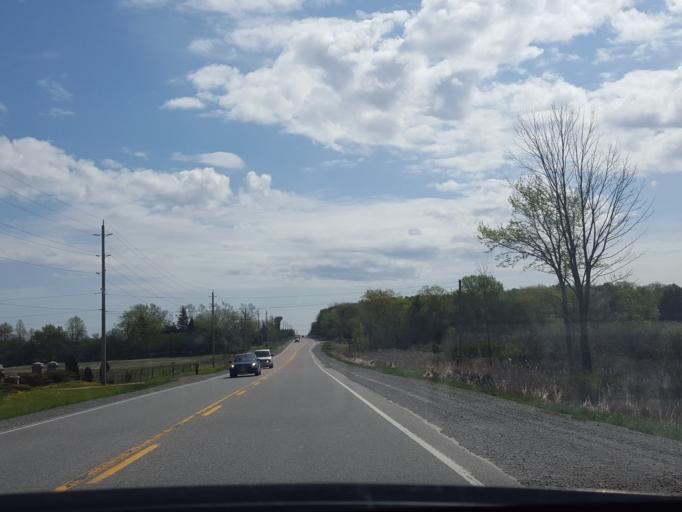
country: CA
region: Ontario
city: Oshawa
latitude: 44.1100
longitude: -78.8636
